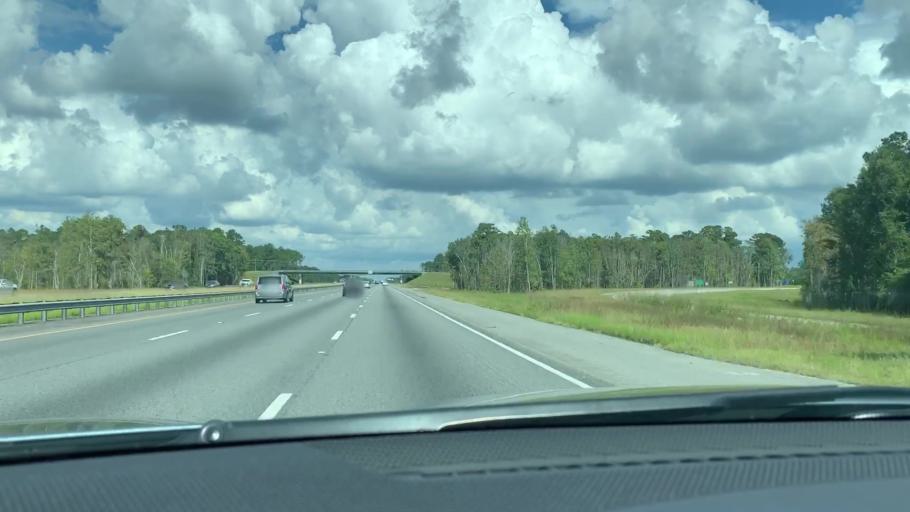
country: US
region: Georgia
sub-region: Glynn County
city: Brunswick
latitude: 31.0986
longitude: -81.5998
